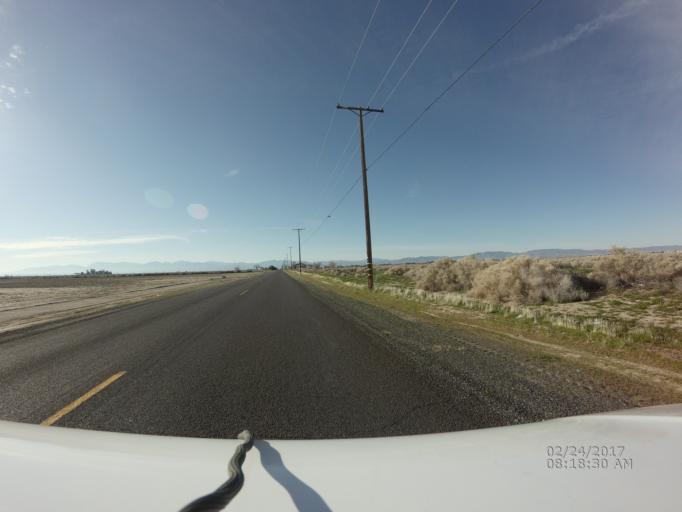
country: US
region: California
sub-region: Los Angeles County
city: Lancaster
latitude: 34.7152
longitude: -118.0413
